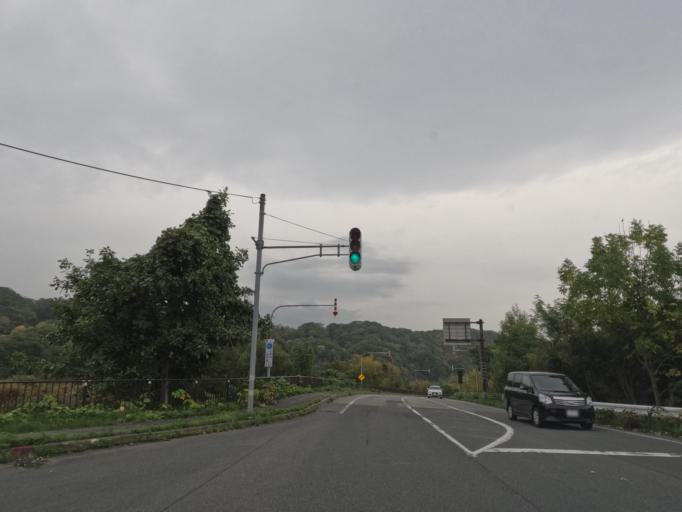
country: JP
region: Hokkaido
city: Date
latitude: 42.5202
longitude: 140.8624
